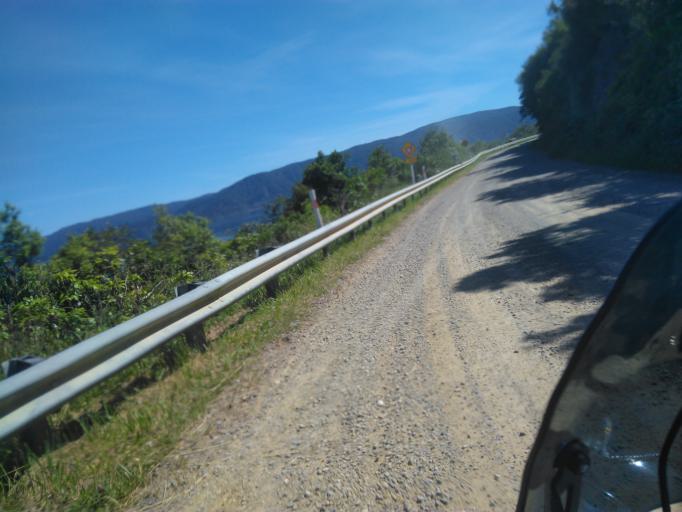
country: NZ
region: Hawke's Bay
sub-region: Wairoa District
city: Wairoa
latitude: -38.7934
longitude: 177.1243
